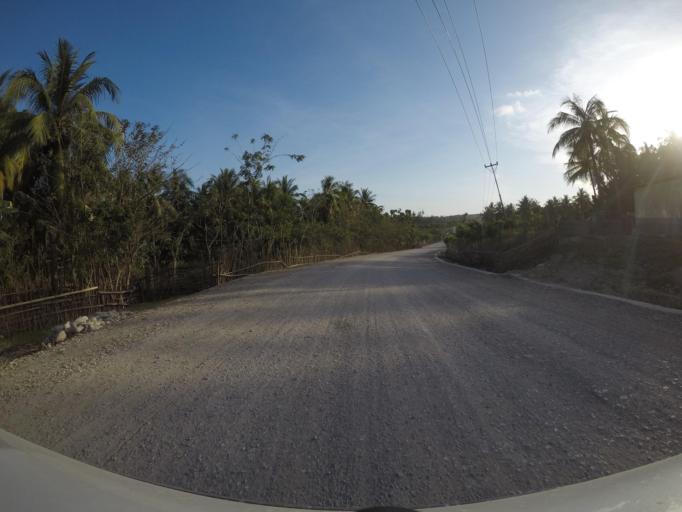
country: TL
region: Viqueque
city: Viqueque
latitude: -8.8281
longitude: 126.5268
